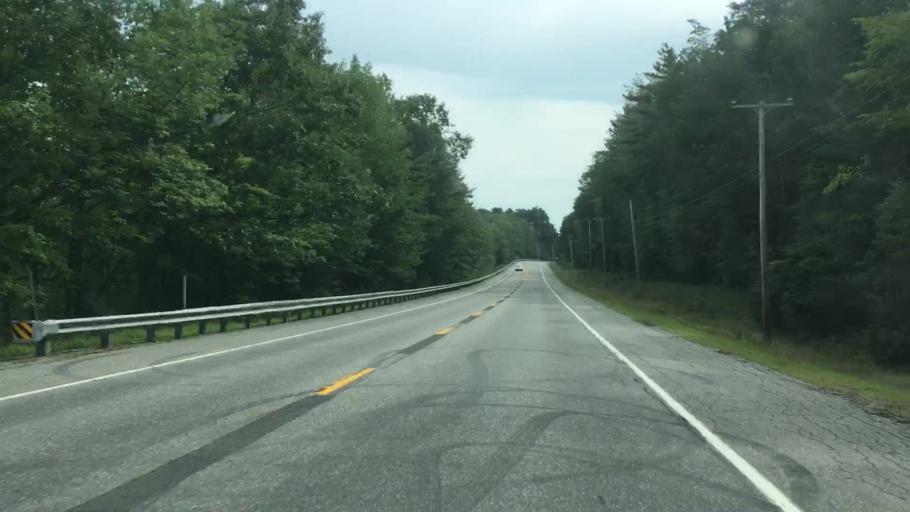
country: US
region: Maine
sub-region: Oxford County
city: Bethel
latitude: 44.4727
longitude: -70.7979
